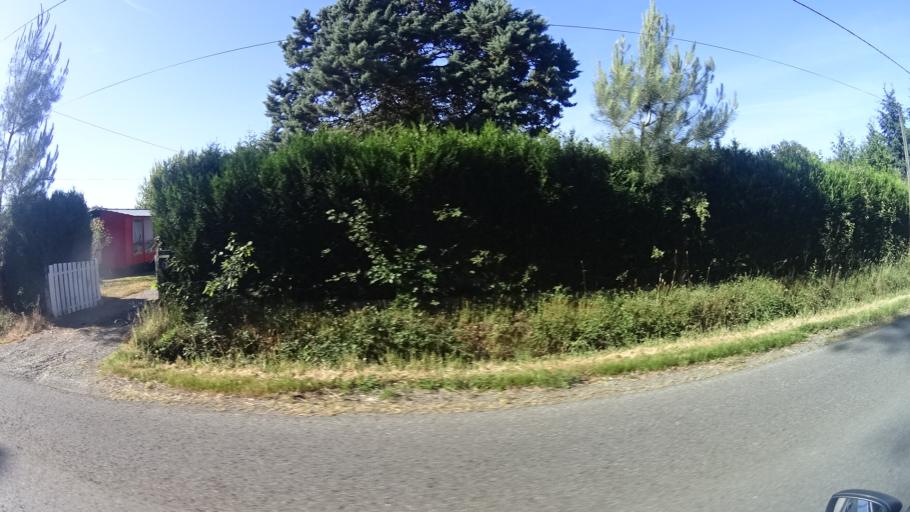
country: FR
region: Brittany
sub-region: Departement d'Ille-et-Vilaine
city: Langon
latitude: 47.7415
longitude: -1.8143
